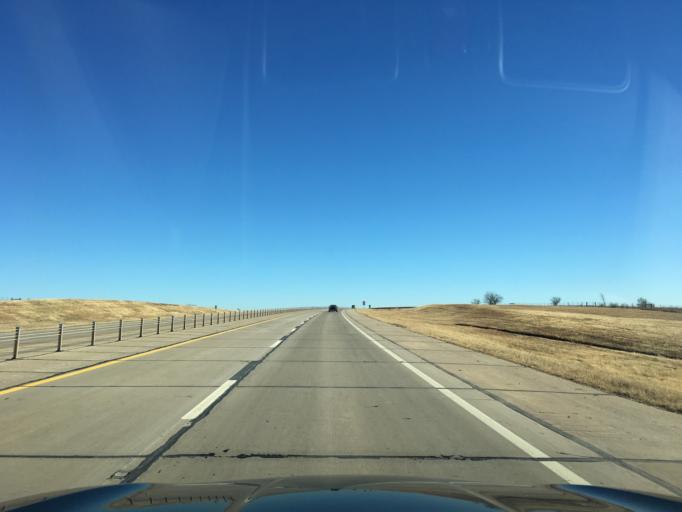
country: US
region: Oklahoma
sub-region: Noble County
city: Perry
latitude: 36.4025
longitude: -97.2580
